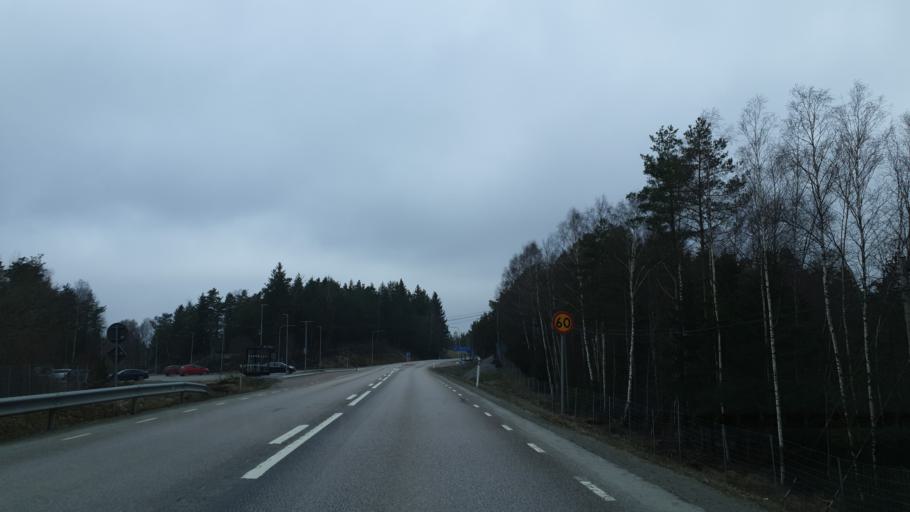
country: SE
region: Vaestra Goetaland
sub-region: Harryda Kommun
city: Hindas
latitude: 57.6716
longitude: 12.3565
